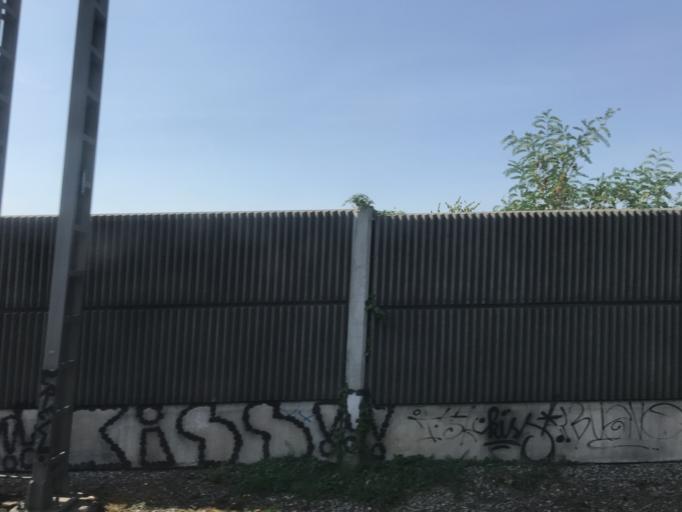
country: CZ
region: Central Bohemia
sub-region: Okres Praha-Vychod
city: Ricany
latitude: 50.0105
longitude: 14.6362
